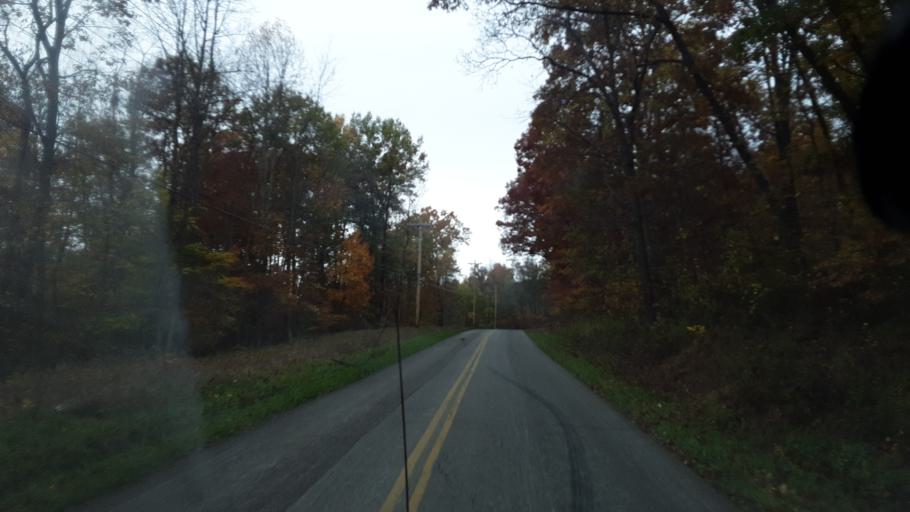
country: US
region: Ohio
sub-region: Holmes County
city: Millersburg
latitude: 40.4830
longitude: -81.9274
